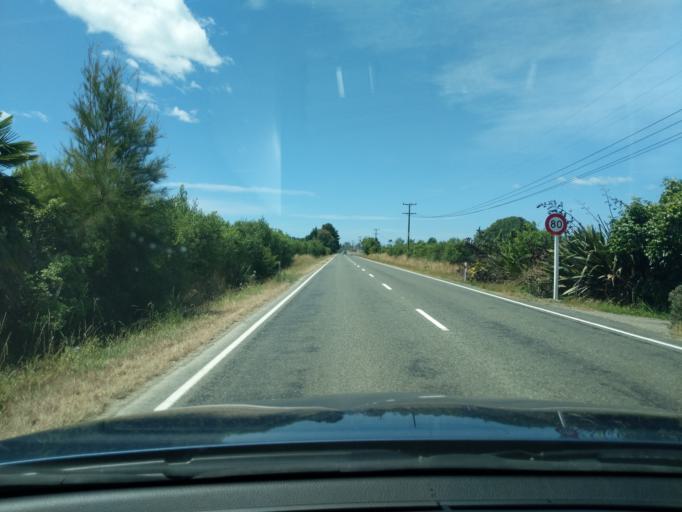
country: NZ
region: Tasman
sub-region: Tasman District
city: Motueka
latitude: -41.0700
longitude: 172.9920
